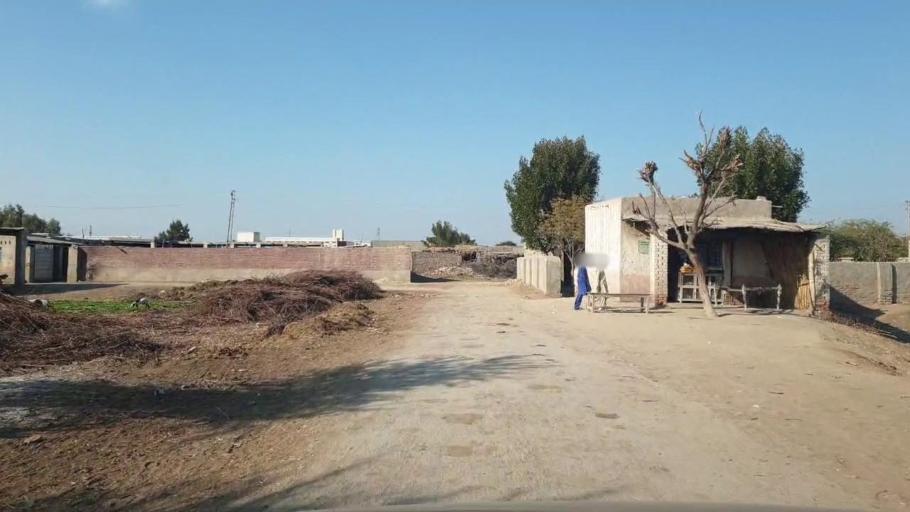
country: PK
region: Sindh
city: Shahpur Chakar
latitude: 26.1764
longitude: 68.6779
